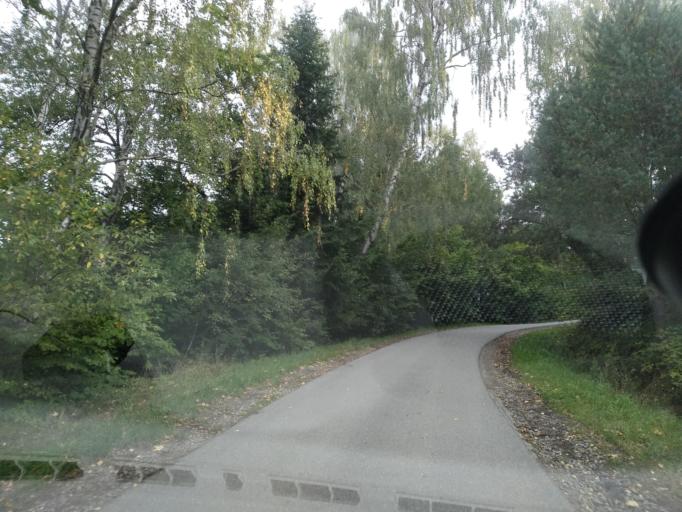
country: PL
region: Lesser Poland Voivodeship
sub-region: Powiat gorlicki
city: Uscie Gorlickie
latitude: 49.5332
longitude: 21.1671
